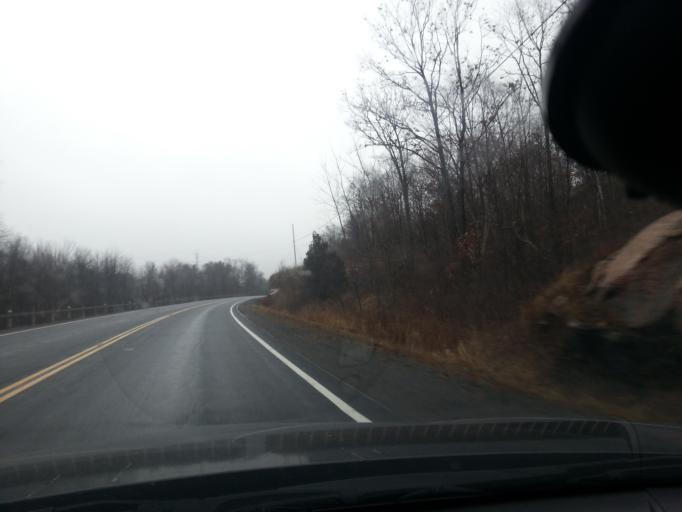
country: CA
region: Ontario
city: Deseronto
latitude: 44.5961
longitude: -77.1894
